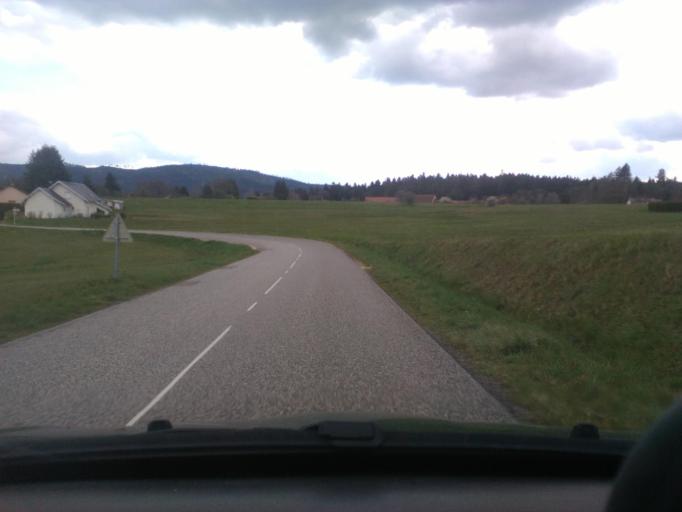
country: FR
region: Lorraine
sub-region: Departement des Vosges
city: Etival-Clairefontaine
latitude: 48.3281
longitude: 6.8255
